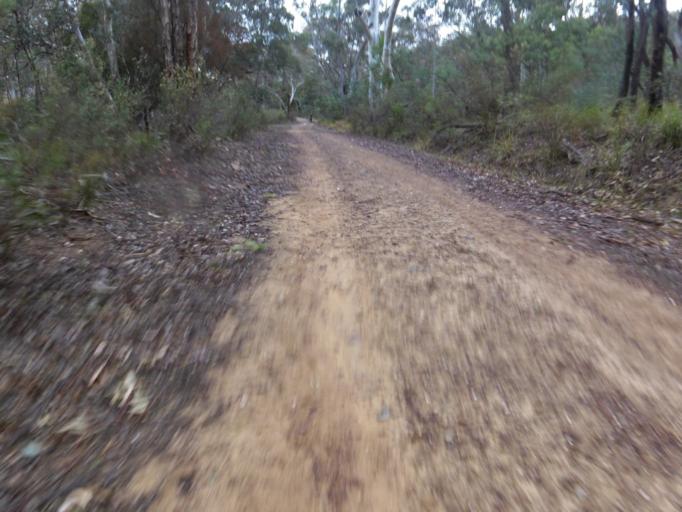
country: AU
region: Australian Capital Territory
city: Macquarie
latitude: -35.2694
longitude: 149.0850
